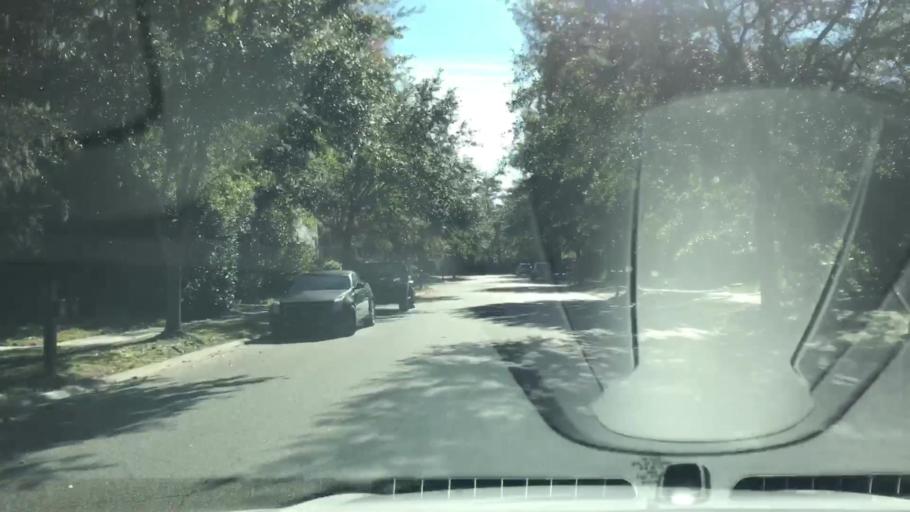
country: US
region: South Carolina
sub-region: Beaufort County
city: Bluffton
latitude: 32.2714
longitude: -80.8751
